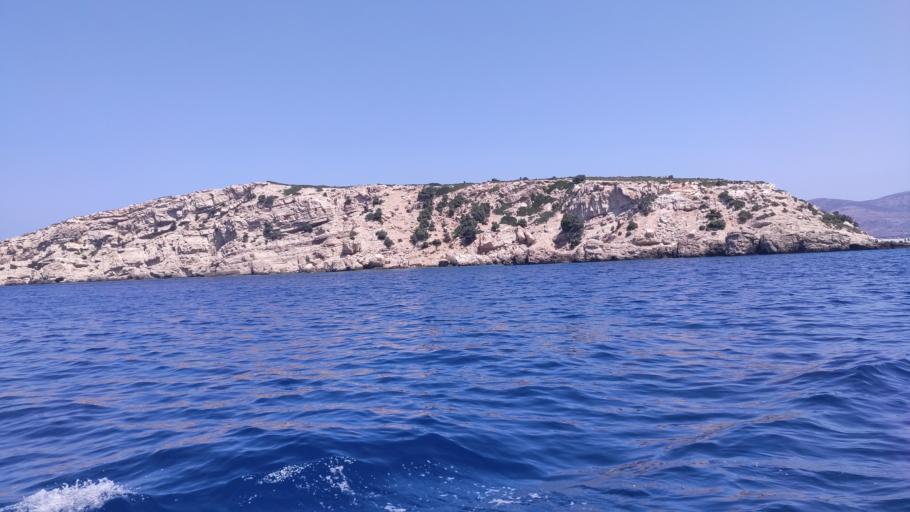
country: GR
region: South Aegean
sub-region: Nomos Dodekanisou
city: Pylion
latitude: 36.9327
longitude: 27.0925
